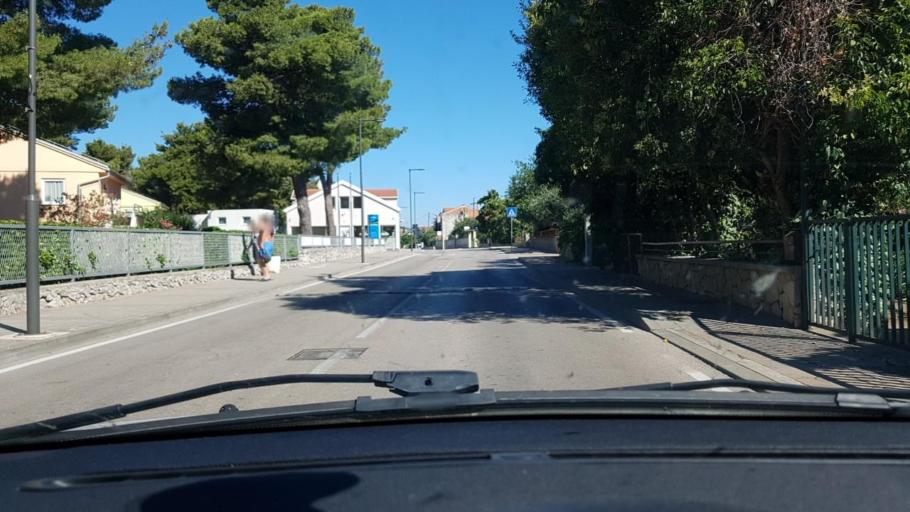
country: HR
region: Sibensko-Kniniska
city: Vodice
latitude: 43.7574
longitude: 15.7851
